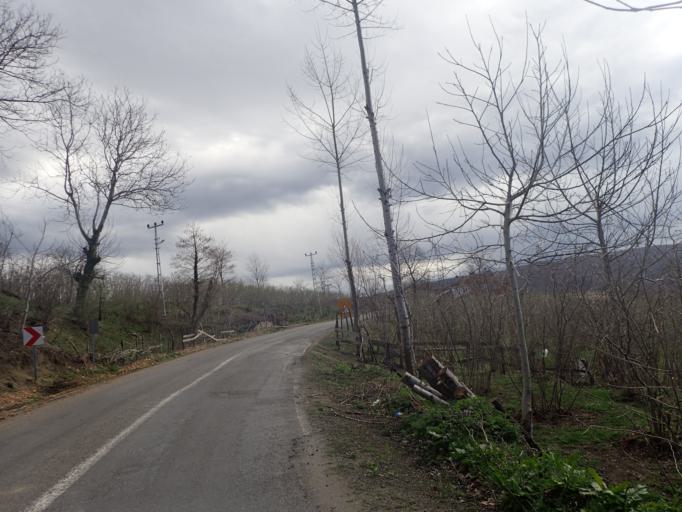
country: TR
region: Ordu
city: Kumru
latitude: 40.9311
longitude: 37.2582
